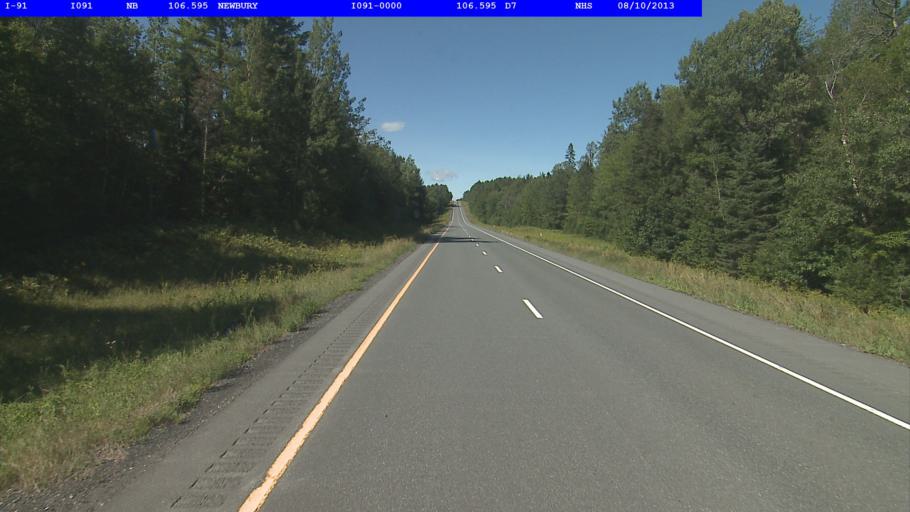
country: US
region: New Hampshire
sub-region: Grafton County
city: Woodsville
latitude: 44.1082
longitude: -72.1075
